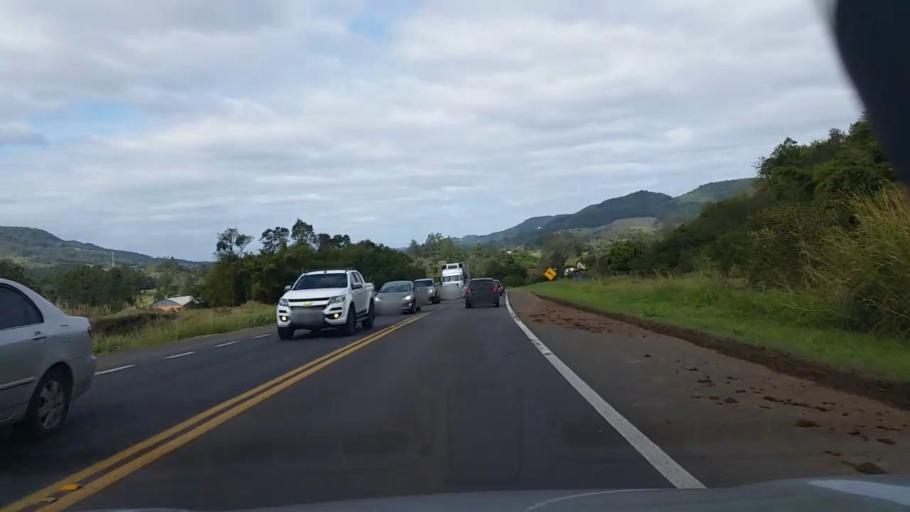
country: BR
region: Rio Grande do Sul
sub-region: Arroio Do Meio
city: Arroio do Meio
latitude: -29.3391
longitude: -52.0789
